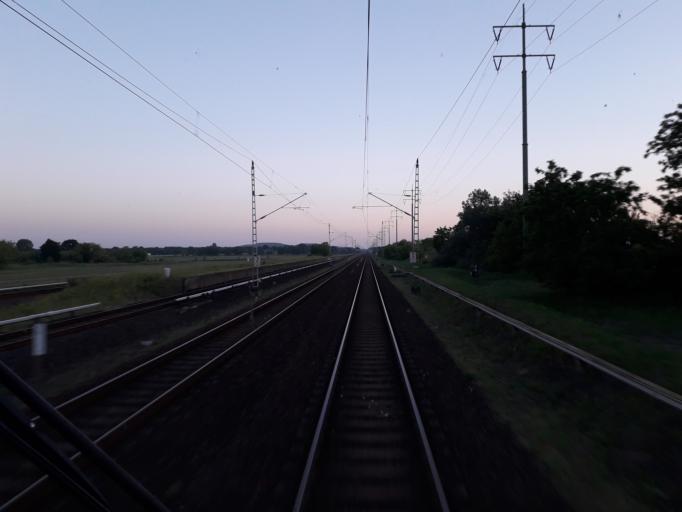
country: DE
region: Berlin
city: Buchholz
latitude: 52.6174
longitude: 13.4456
